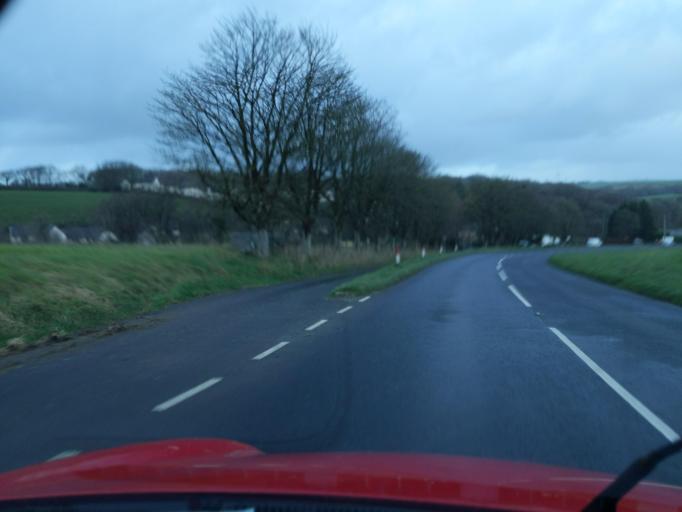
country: GB
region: England
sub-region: Devon
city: Holsworthy
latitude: 50.8875
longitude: -4.2808
